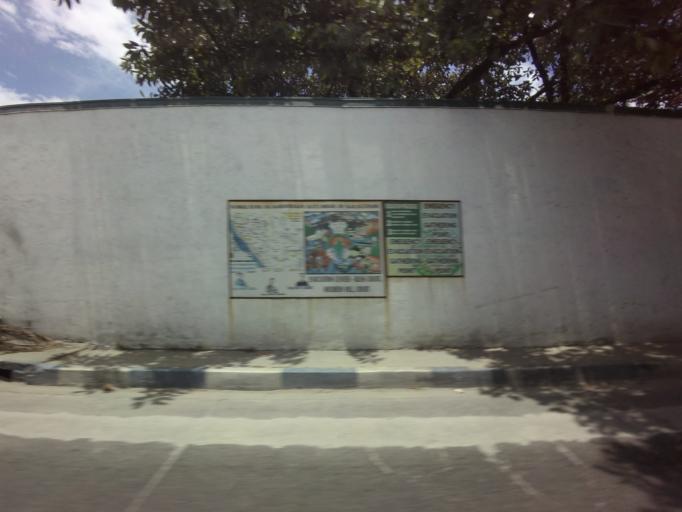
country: PH
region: Calabarzon
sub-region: Province of Rizal
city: Cainta
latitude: 14.5870
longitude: 121.0960
